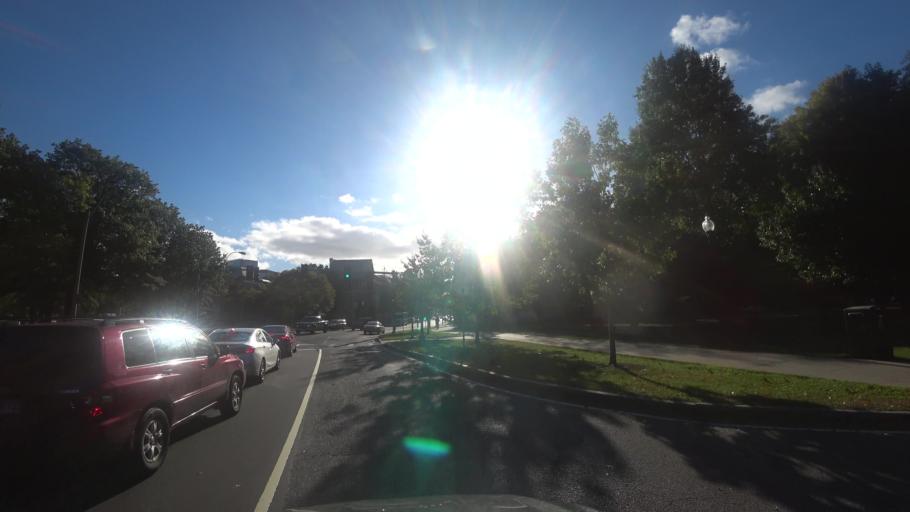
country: US
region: Massachusetts
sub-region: Norfolk County
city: Brookline
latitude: 42.3388
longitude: -71.0984
